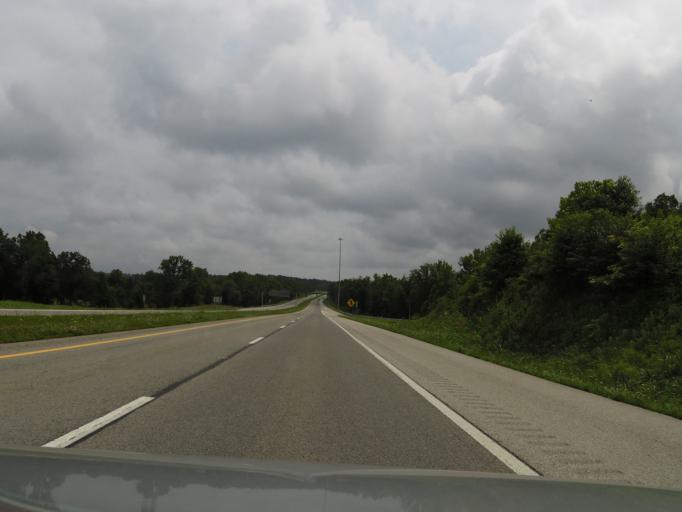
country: US
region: Kentucky
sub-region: Ohio County
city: Oak Grove
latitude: 37.3858
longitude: -86.8064
